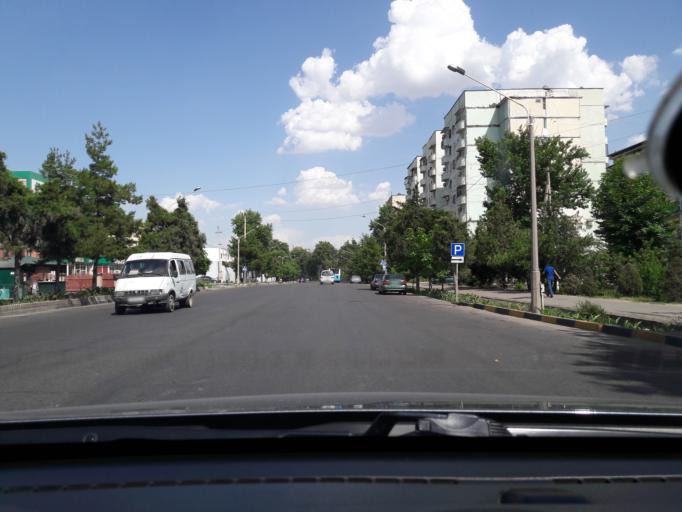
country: TJ
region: Dushanbe
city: Dushanbe
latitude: 38.5188
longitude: 68.7496
